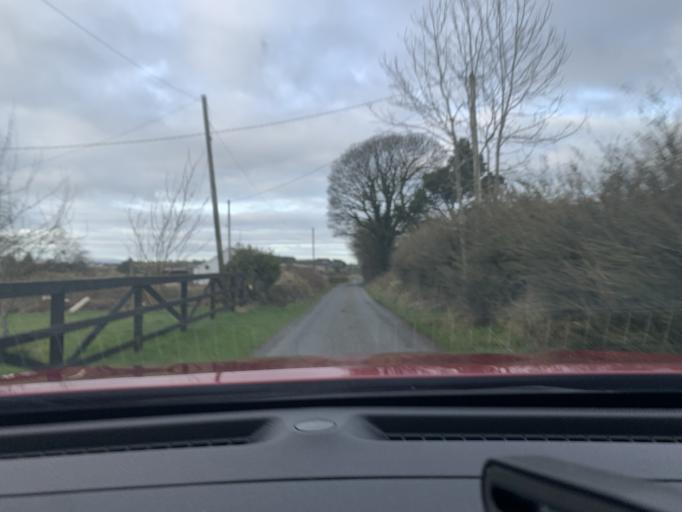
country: IE
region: Connaught
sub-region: Roscommon
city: Ballaghaderreen
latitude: 53.9669
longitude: -8.5594
